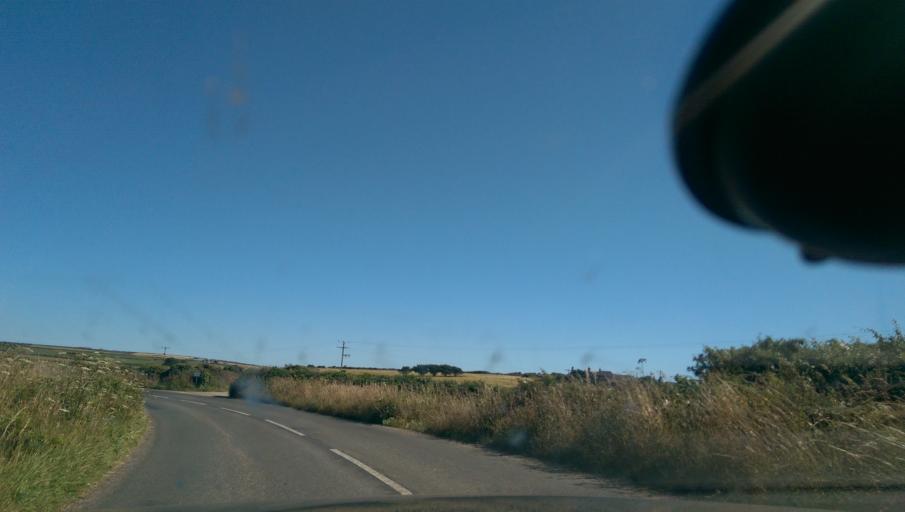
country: GB
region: England
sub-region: Cornwall
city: Sennen
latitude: 50.0644
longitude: -5.6926
